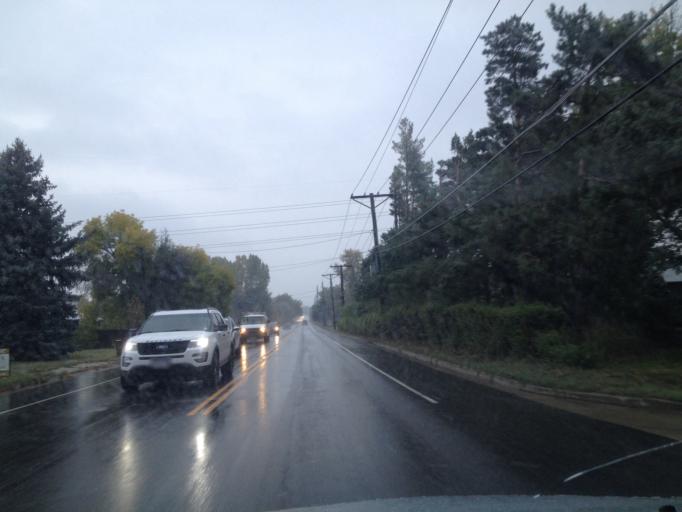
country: US
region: Colorado
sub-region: Boulder County
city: Superior
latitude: 39.9895
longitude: -105.1753
